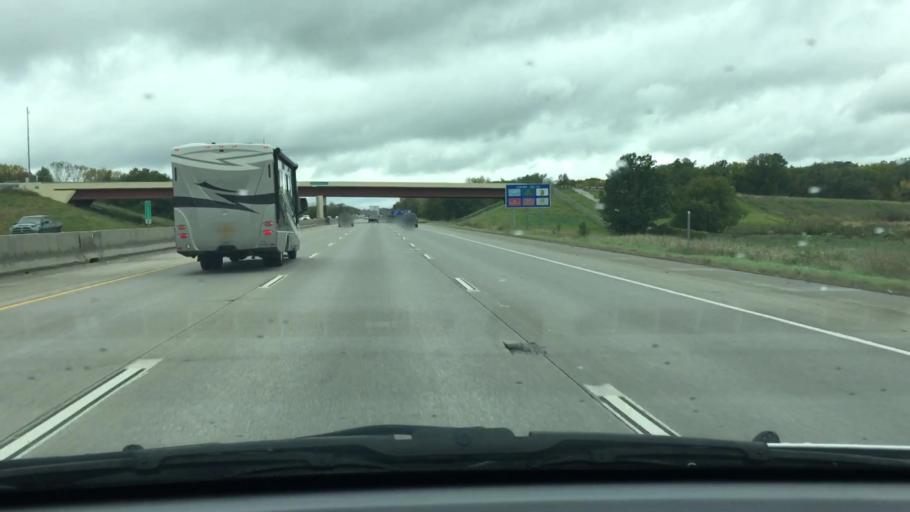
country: US
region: Iowa
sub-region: Polk County
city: Saylorville
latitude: 41.6503
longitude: -93.6502
